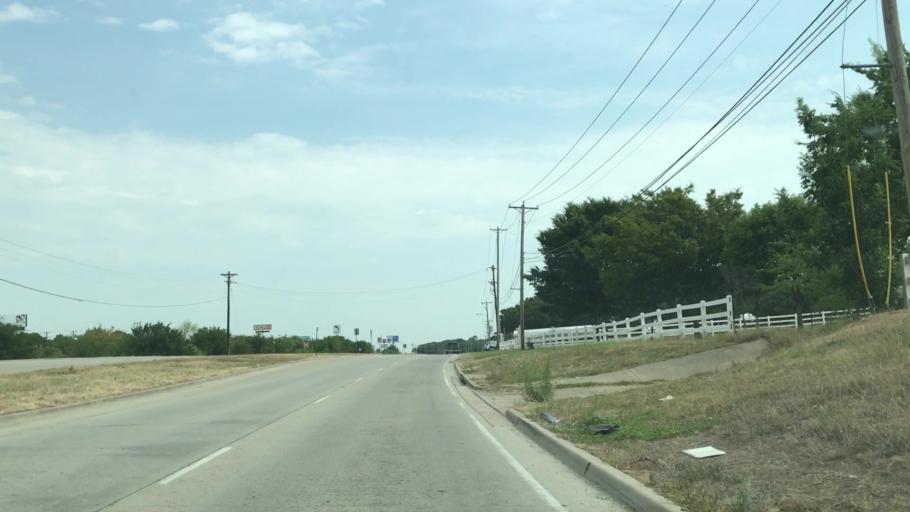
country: US
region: Texas
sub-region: Tarrant County
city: Keller
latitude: 32.9427
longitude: -97.2539
